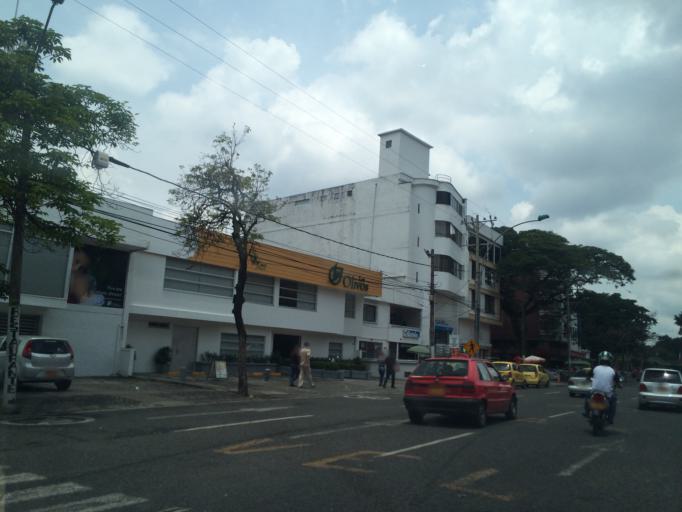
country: CO
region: Valle del Cauca
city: Cali
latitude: 3.4682
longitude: -76.5247
